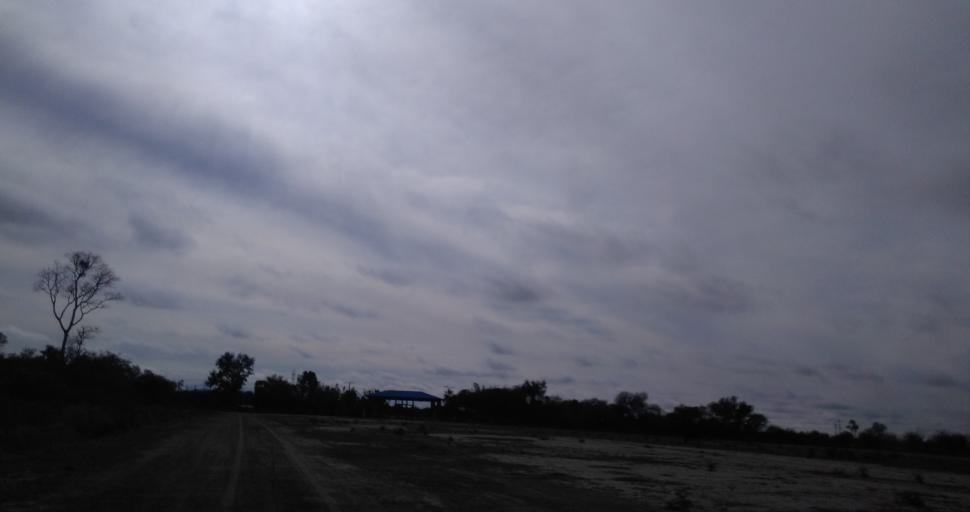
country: AR
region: Chaco
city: Fontana
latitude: -27.3907
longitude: -58.9853
